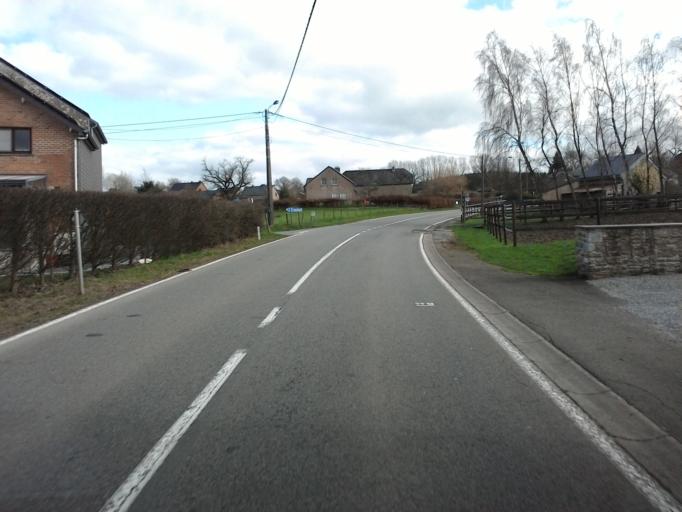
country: BE
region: Wallonia
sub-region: Province de Liege
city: Ferrieres
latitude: 50.3894
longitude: 5.6614
